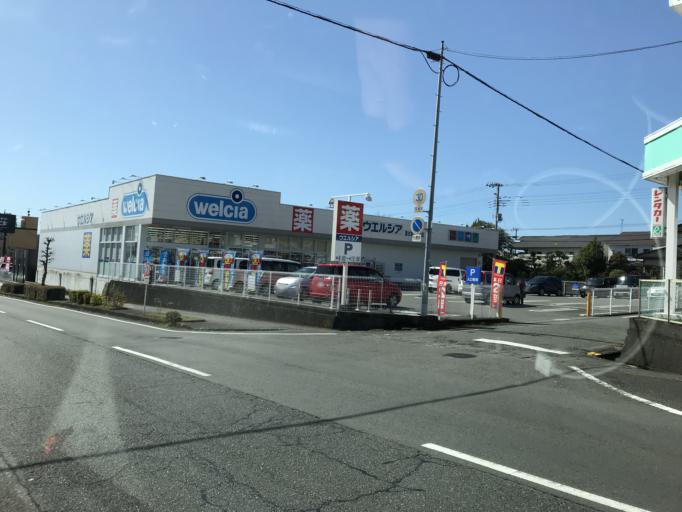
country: JP
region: Shizuoka
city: Fujinomiya
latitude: 35.2171
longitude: 138.6284
